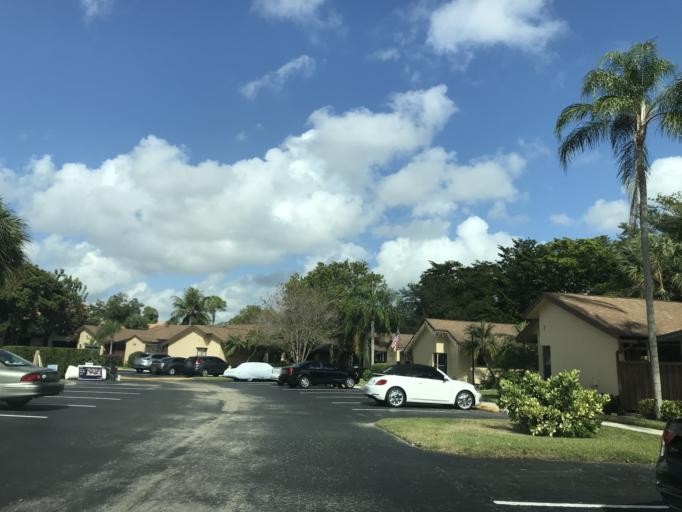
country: US
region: Florida
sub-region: Broward County
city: Coconut Creek
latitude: 26.2704
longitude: -80.1891
